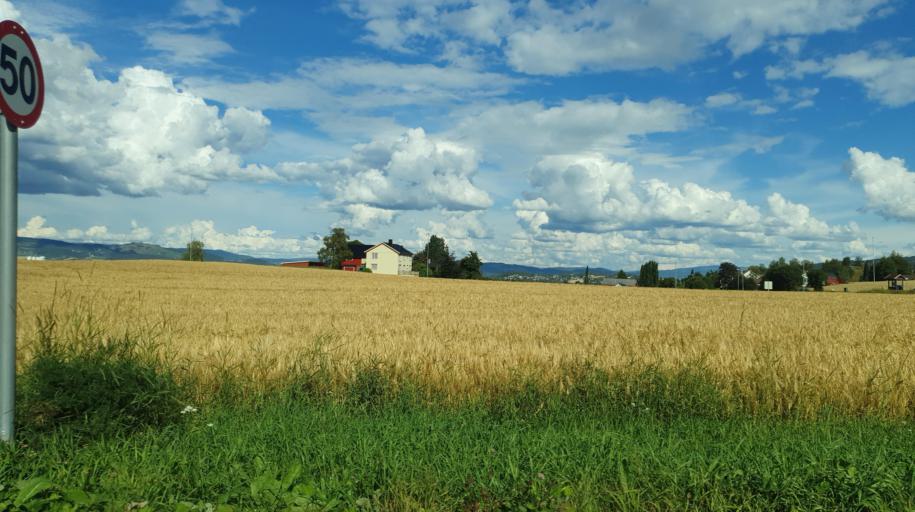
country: NO
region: Nord-Trondelag
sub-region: Verdal
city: Verdal
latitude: 63.7618
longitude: 11.4055
